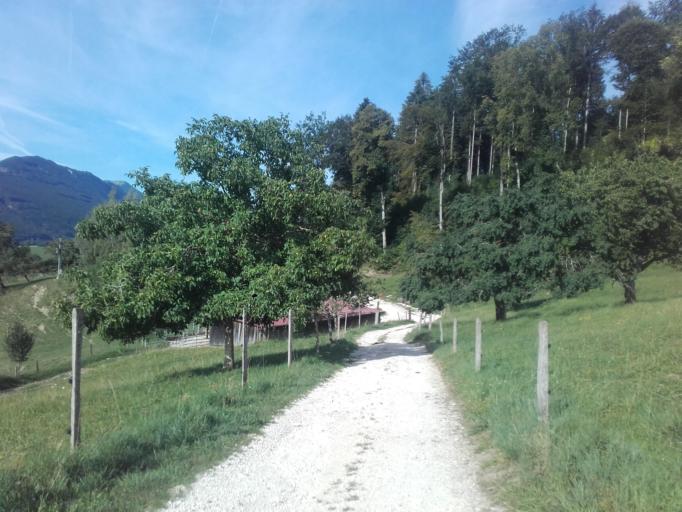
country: CH
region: Solothurn
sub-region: Bezirk Thal
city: Matzendorf
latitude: 47.3164
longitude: 7.6350
